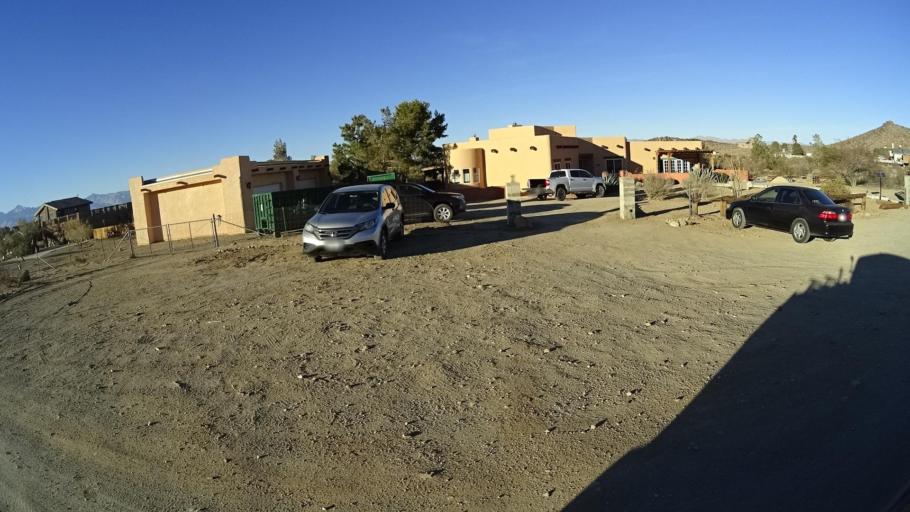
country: US
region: California
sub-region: Kern County
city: Ridgecrest
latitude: 35.5787
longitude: -117.6542
